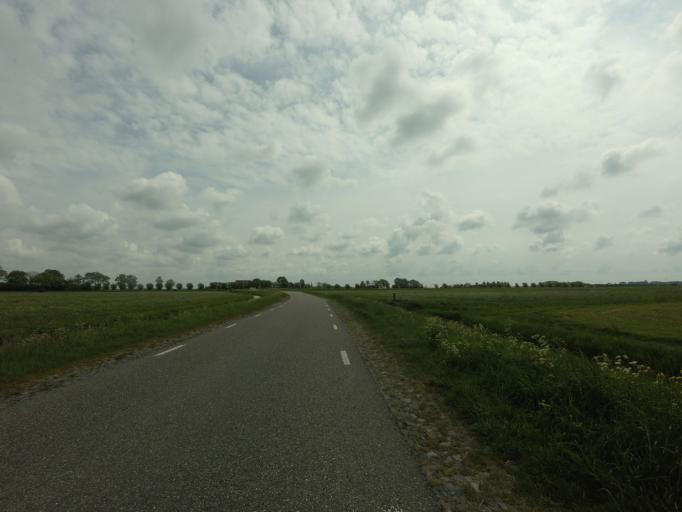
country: NL
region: Friesland
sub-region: Sudwest Fryslan
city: Bolsward
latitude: 53.0948
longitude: 5.5308
